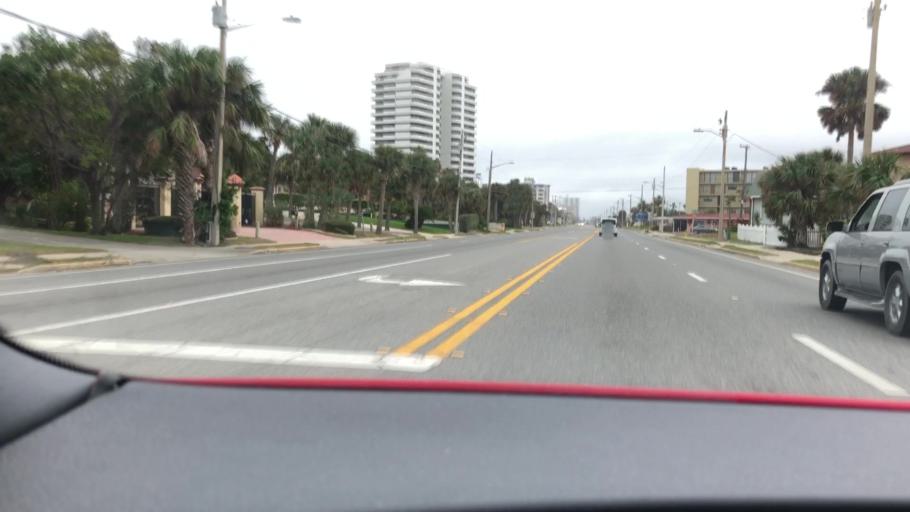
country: US
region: Florida
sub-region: Volusia County
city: Holly Hill
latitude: 29.2524
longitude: -81.0206
